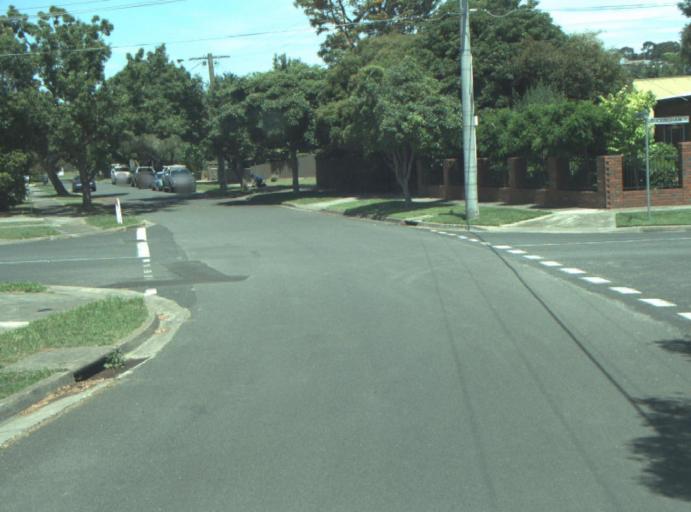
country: AU
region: Victoria
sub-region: Greater Geelong
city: Wandana Heights
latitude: -38.1579
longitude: 144.3241
